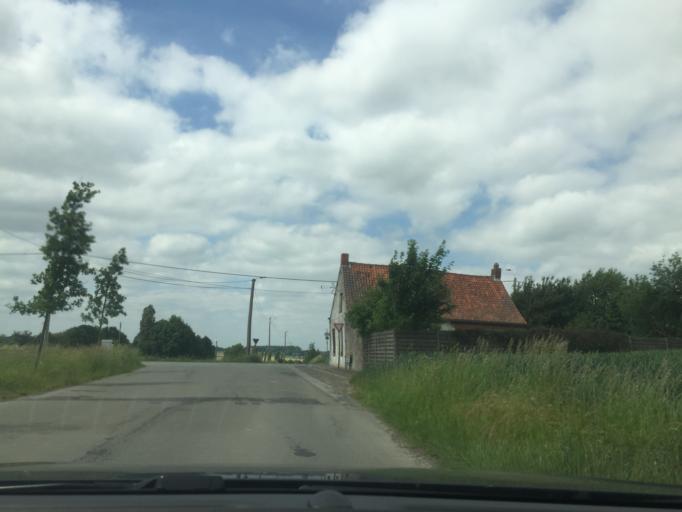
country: BE
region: Flanders
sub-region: Provincie West-Vlaanderen
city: Zwevegem
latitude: 50.7505
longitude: 3.3539
